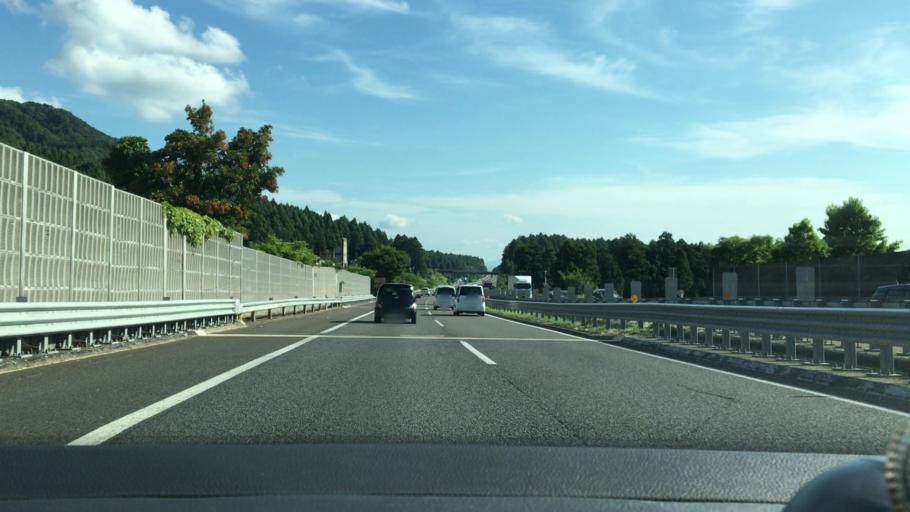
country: JP
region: Fukui
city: Maruoka
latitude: 36.1769
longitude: 136.2958
